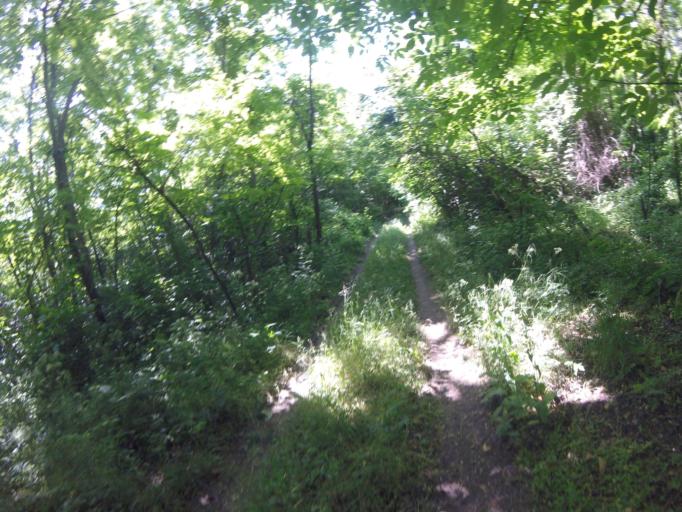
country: HU
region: Zala
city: Zalaszentgrot
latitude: 46.9189
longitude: 17.0437
